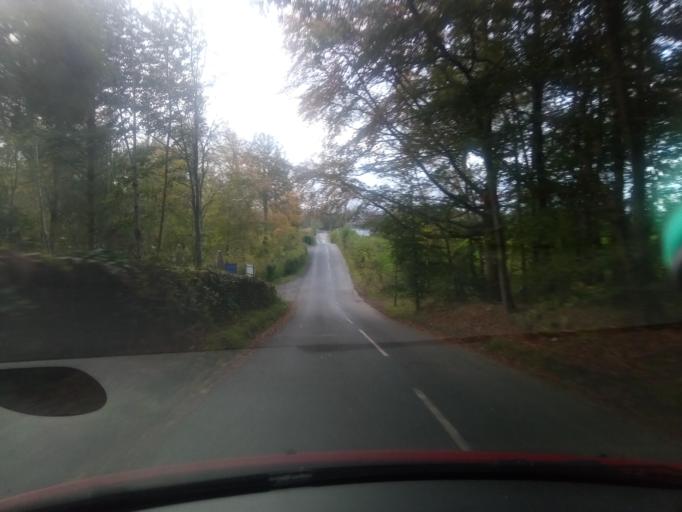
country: GB
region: Scotland
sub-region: The Scottish Borders
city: Jedburgh
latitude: 55.4053
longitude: -2.6552
